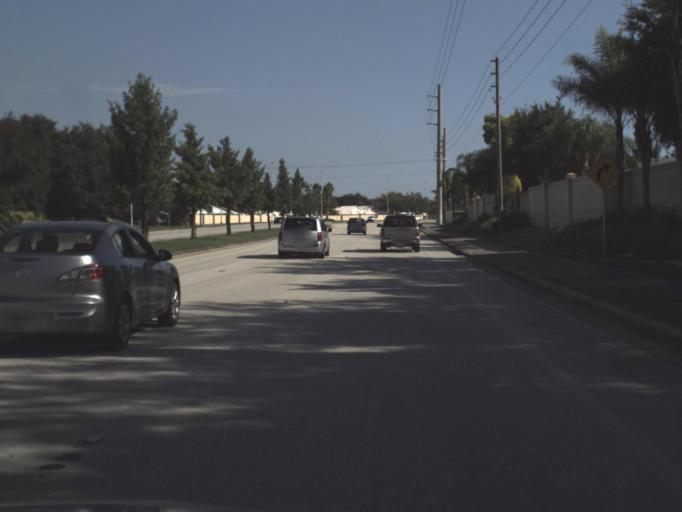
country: US
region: Florida
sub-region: Sarasota County
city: South Venice
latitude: 27.0401
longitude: -82.3996
